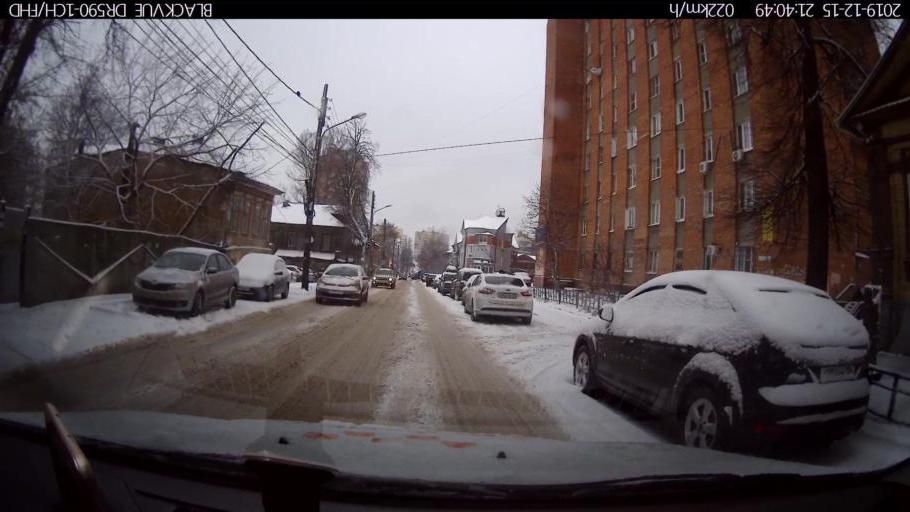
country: RU
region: Nizjnij Novgorod
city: Nizhniy Novgorod
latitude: 56.3198
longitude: 43.9858
